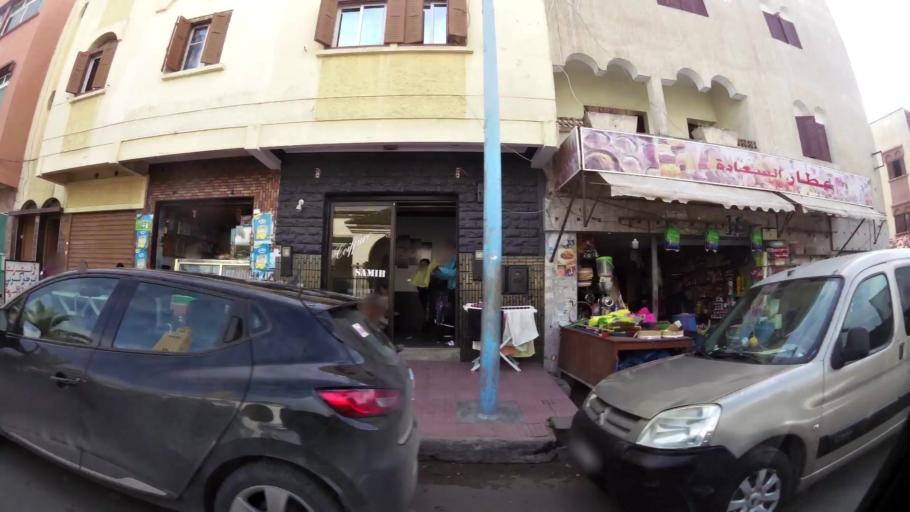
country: MA
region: Doukkala-Abda
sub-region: El-Jadida
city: El Jadida
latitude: 33.2432
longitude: -8.5257
